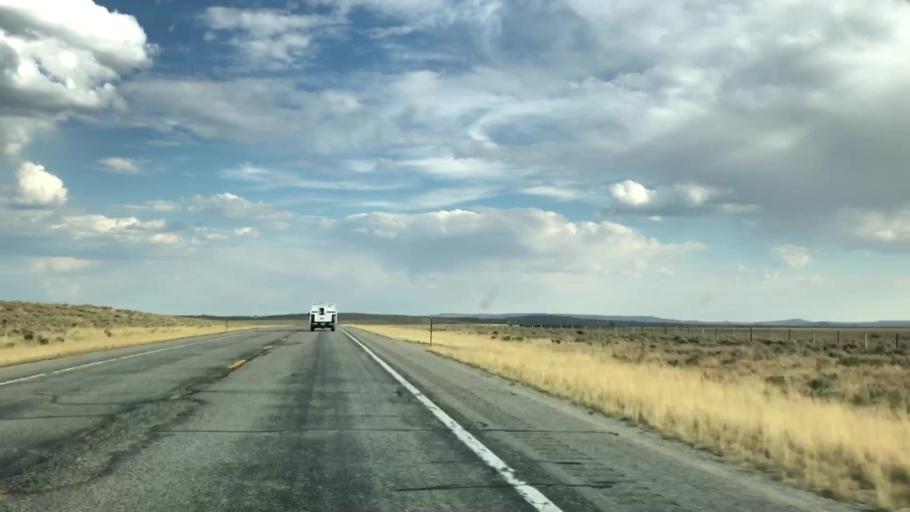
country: US
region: Wyoming
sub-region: Sublette County
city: Pinedale
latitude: 43.0380
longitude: -110.1360
